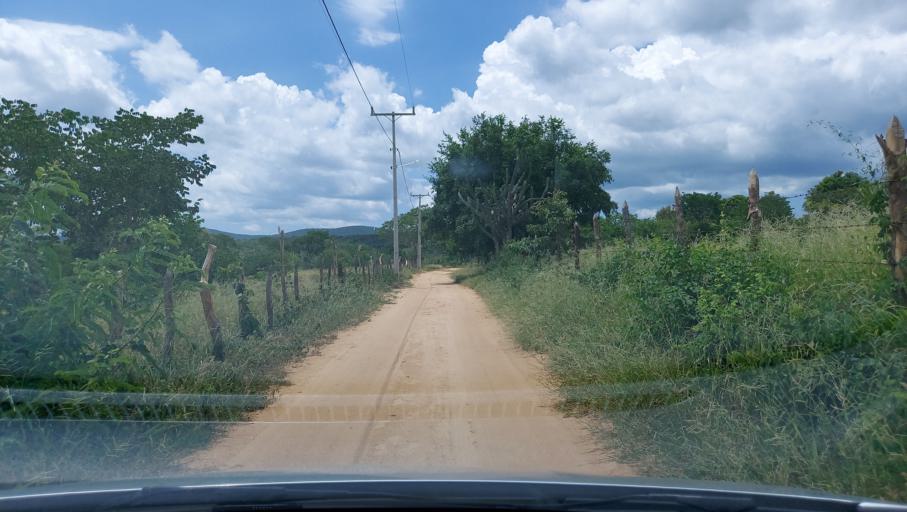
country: BR
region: Bahia
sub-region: Oliveira Dos Brejinhos
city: Beira Rio
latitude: -12.0185
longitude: -42.6308
